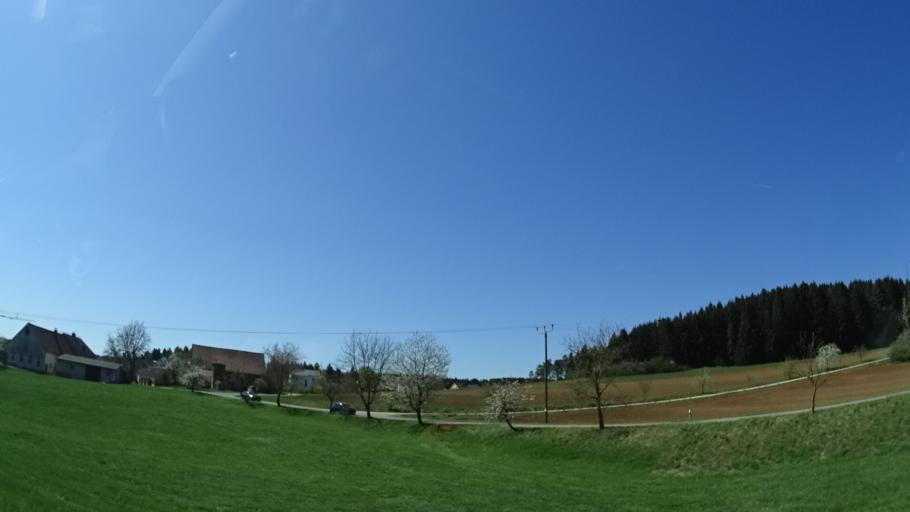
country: DE
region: Bavaria
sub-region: Upper Palatinate
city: Lauterhofen
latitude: 49.4078
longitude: 11.6176
